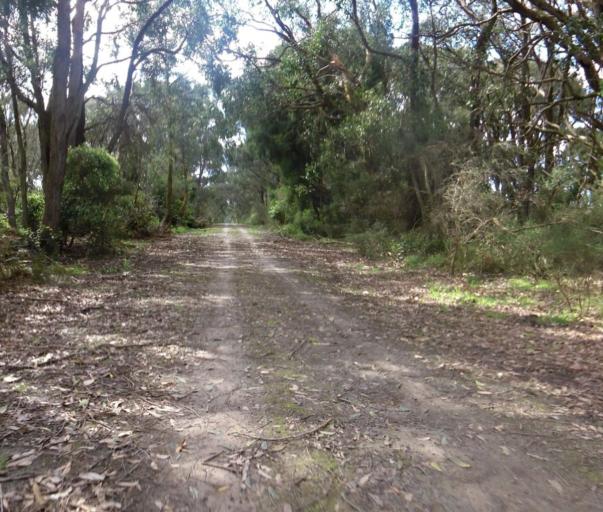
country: AU
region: Victoria
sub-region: Bass Coast
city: North Wonthaggi
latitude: -38.6243
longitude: 146.0392
